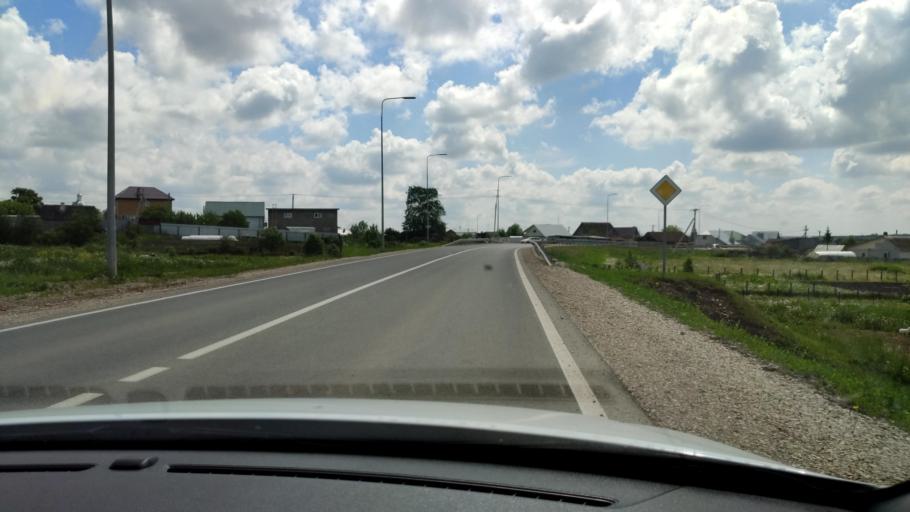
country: RU
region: Tatarstan
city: Vysokaya Gora
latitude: 55.9997
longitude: 49.2987
